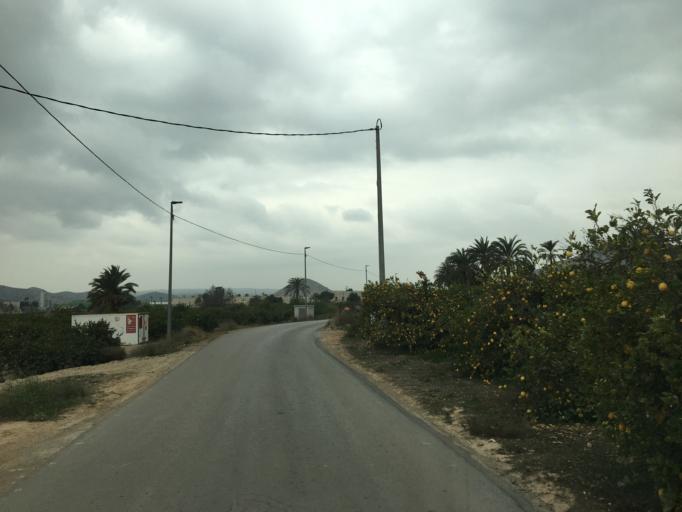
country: ES
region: Murcia
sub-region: Murcia
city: Santomera
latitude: 38.0792
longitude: -1.0482
